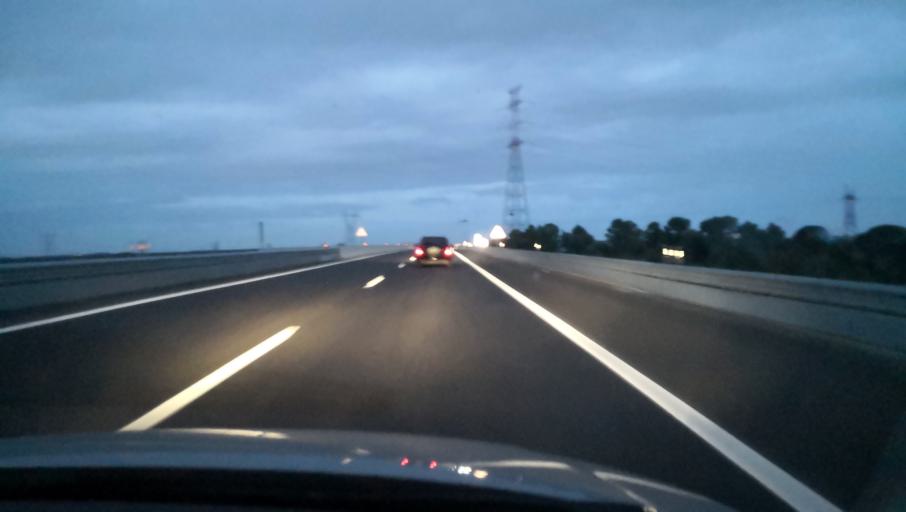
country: PT
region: Setubal
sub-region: Seixal
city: Aldeia de Paio Pires
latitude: 38.5881
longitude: -9.0635
